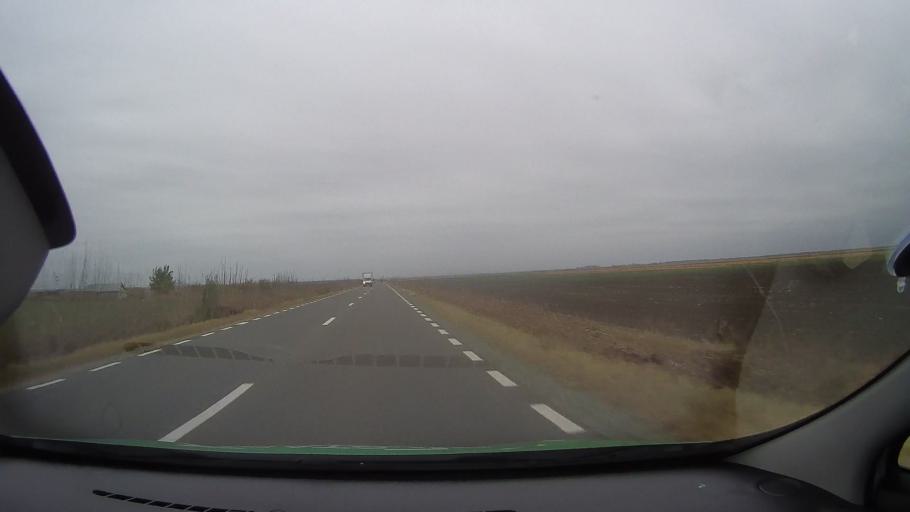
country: RO
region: Ialomita
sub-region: Comuna Gheorghe Lazar
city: Gheorghe Lazar
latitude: 44.6425
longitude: 27.4027
